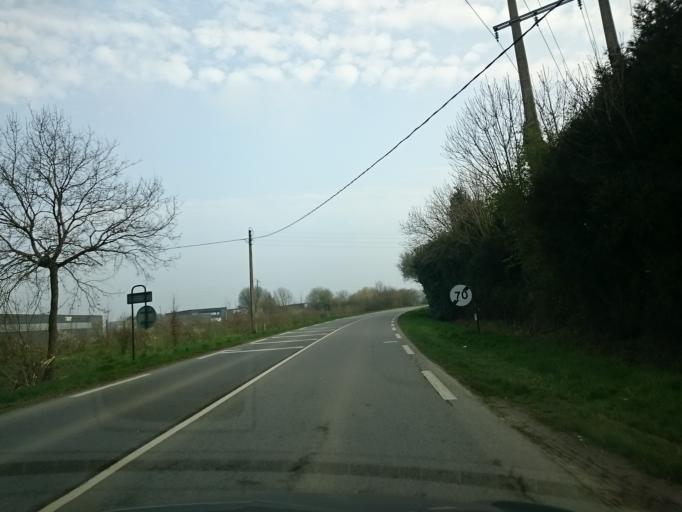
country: FR
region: Brittany
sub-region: Departement d'Ille-et-Vilaine
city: Chatillon-sur-Seiche
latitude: 48.0701
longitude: -1.6657
